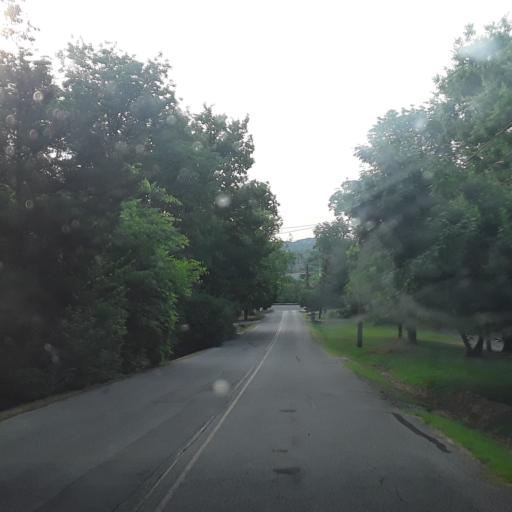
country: US
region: Tennessee
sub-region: Williamson County
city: Brentwood
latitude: 36.0564
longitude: -86.7778
